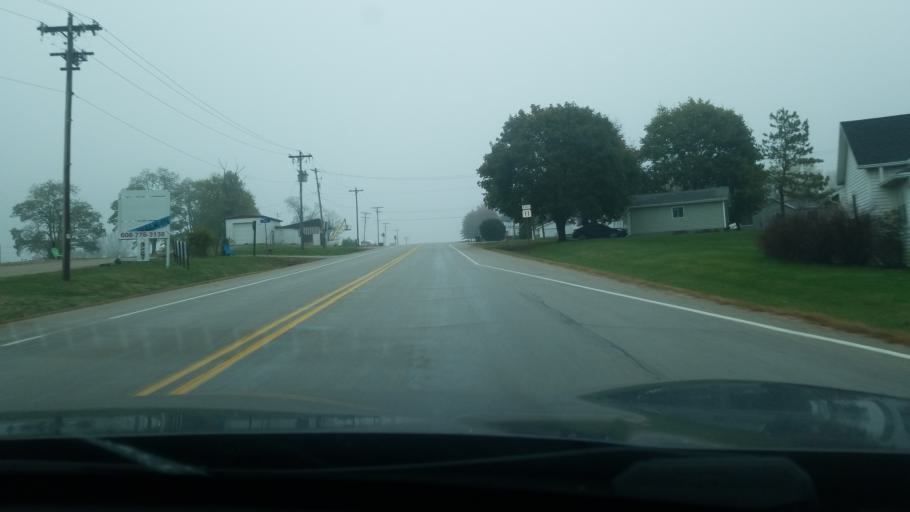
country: US
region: Wisconsin
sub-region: Lafayette County
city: Shullsburg
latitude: 42.5757
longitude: -90.2365
